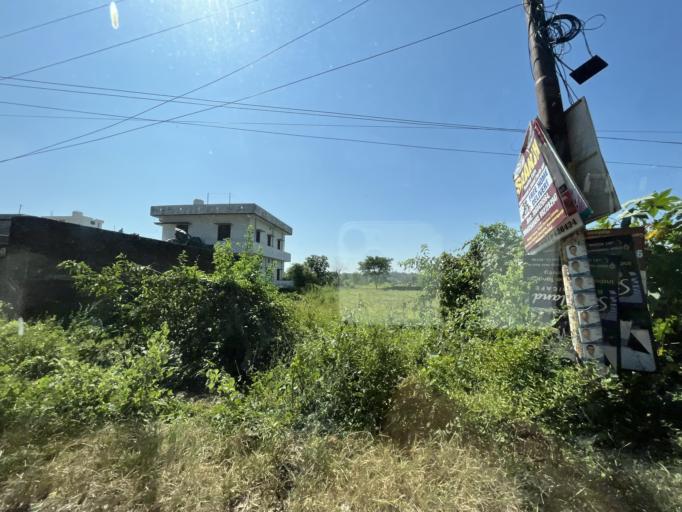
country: IN
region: Uttarakhand
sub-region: Naini Tal
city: Haldwani
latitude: 29.2119
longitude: 79.4598
